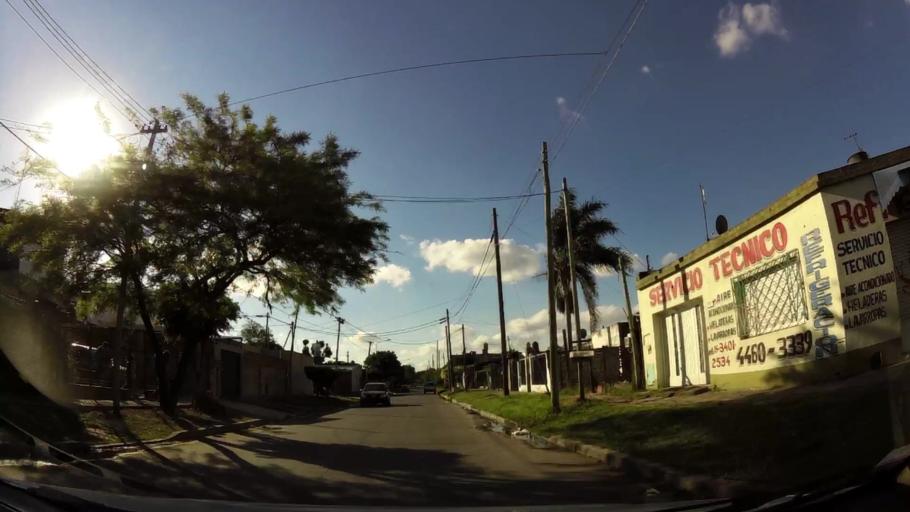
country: AR
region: Buenos Aires
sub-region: Partido de Moron
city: Moron
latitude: -34.6795
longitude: -58.6104
